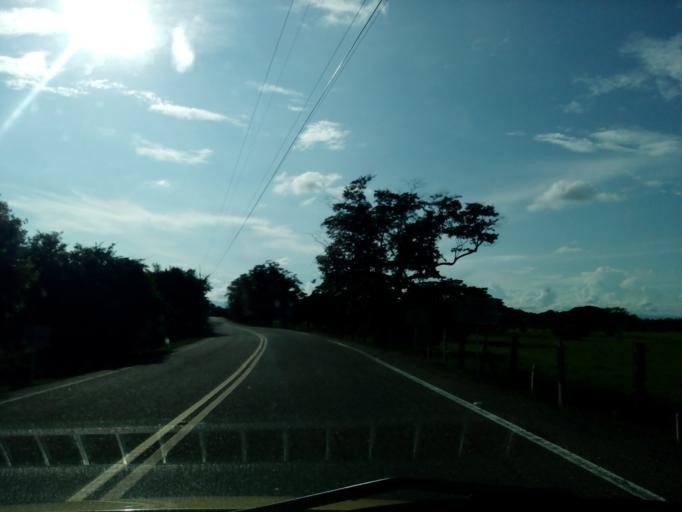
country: CO
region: Boyaca
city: Puerto Boyaca
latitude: 5.9406
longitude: -74.5608
